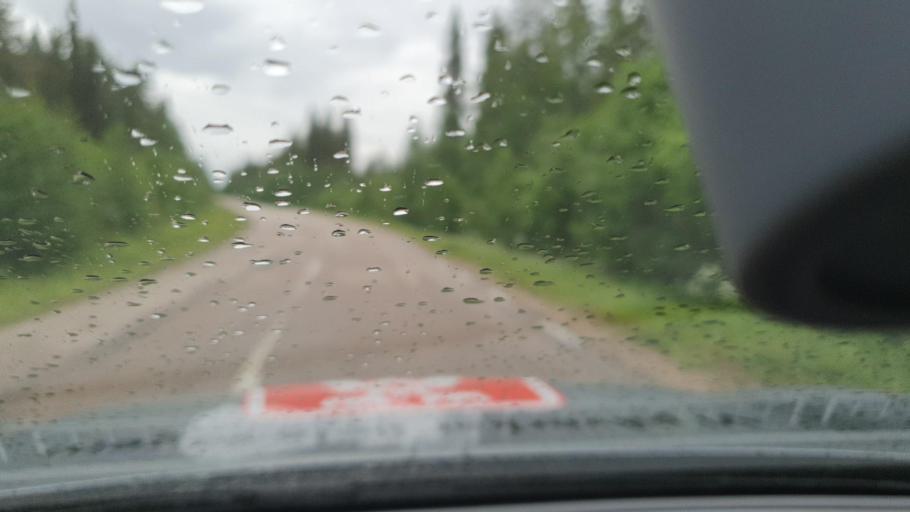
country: SE
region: Norrbotten
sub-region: Overkalix Kommun
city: OEverkalix
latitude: 66.4518
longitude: 22.7710
